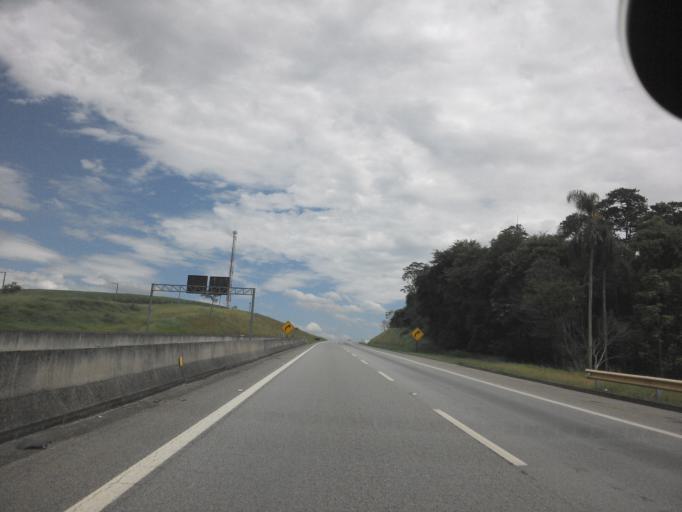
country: BR
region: Sao Paulo
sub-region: Cacapava
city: Cacapava
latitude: -23.1649
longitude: -45.7047
